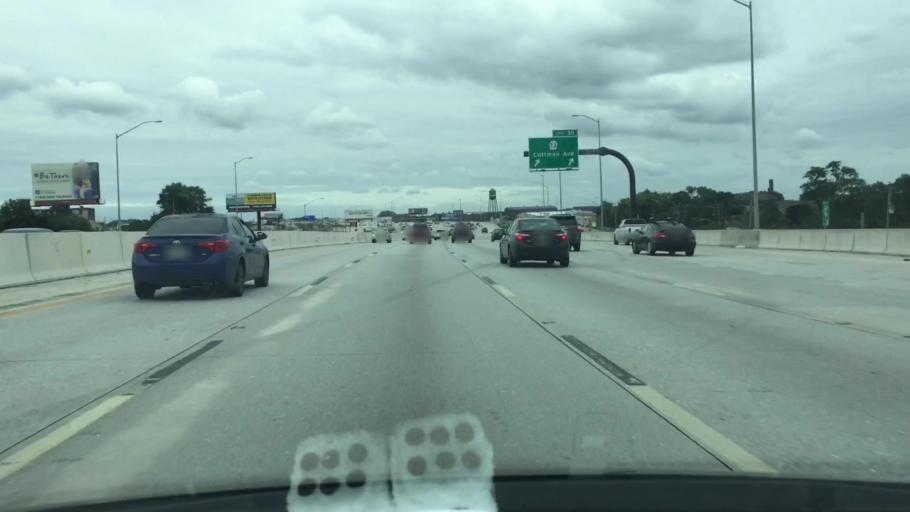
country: US
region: New Jersey
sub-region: Burlington County
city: Palmyra
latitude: 40.0232
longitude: -75.0381
